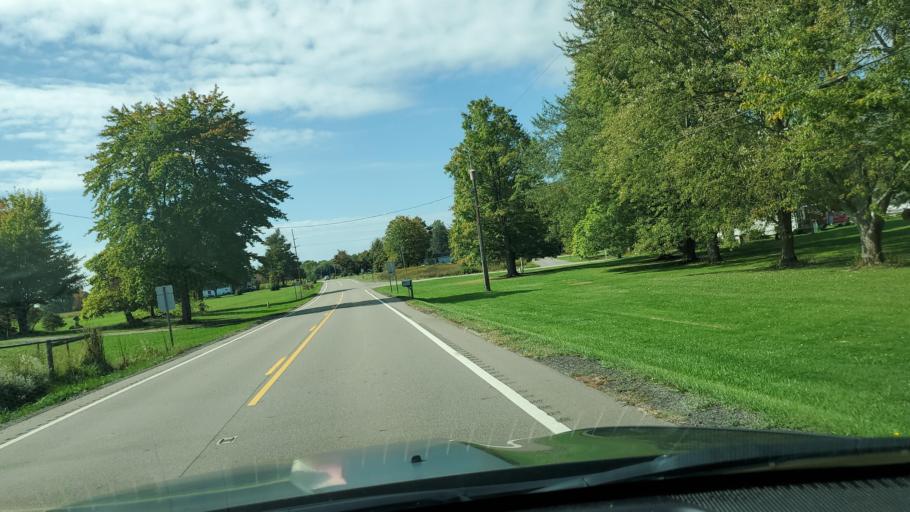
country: US
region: Ohio
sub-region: Trumbull County
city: Cortland
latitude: 41.4031
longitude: -80.6169
